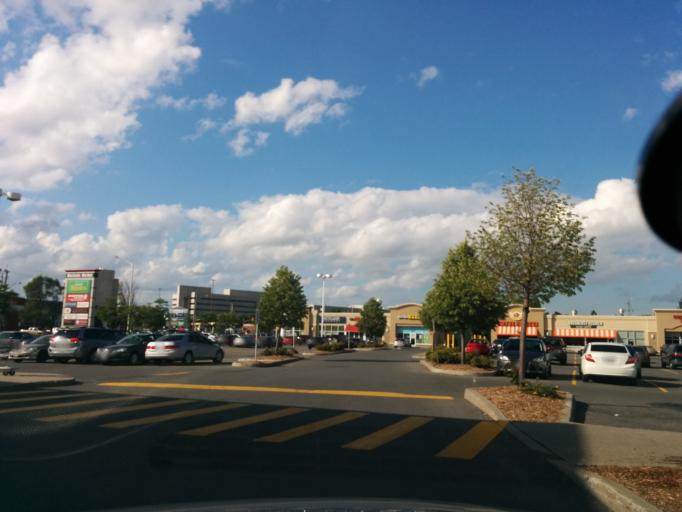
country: CA
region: Ontario
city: Ottawa
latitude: 45.3606
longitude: -75.7340
